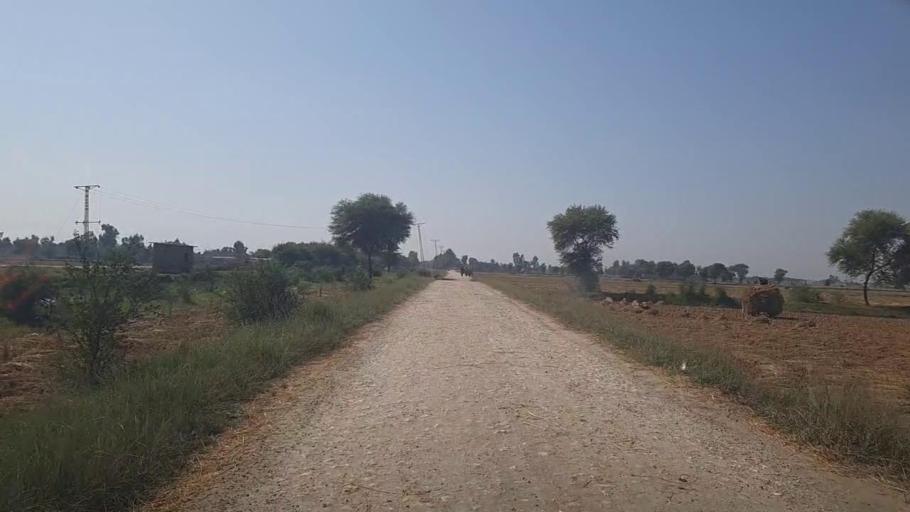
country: PK
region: Sindh
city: Thul
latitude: 28.2502
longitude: 68.8118
